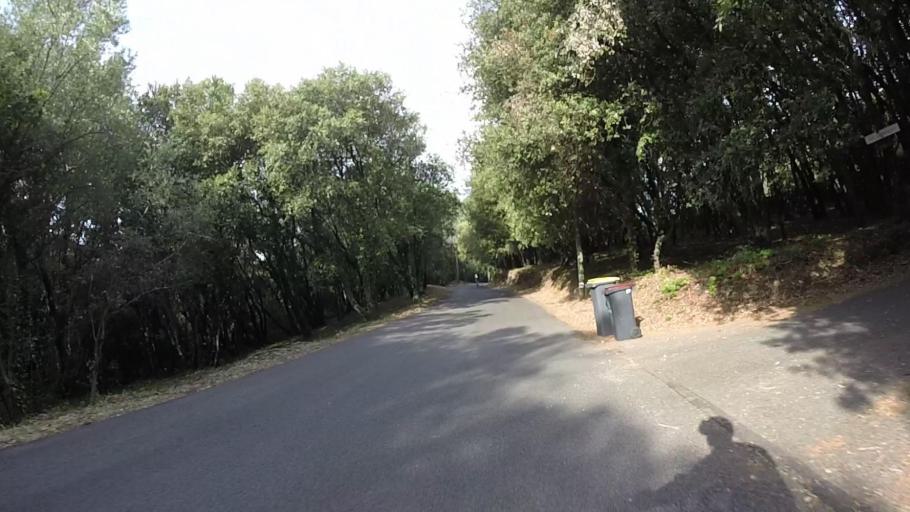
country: FR
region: Provence-Alpes-Cote d'Azur
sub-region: Departement des Alpes-Maritimes
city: Biot
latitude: 43.6194
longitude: 7.0943
